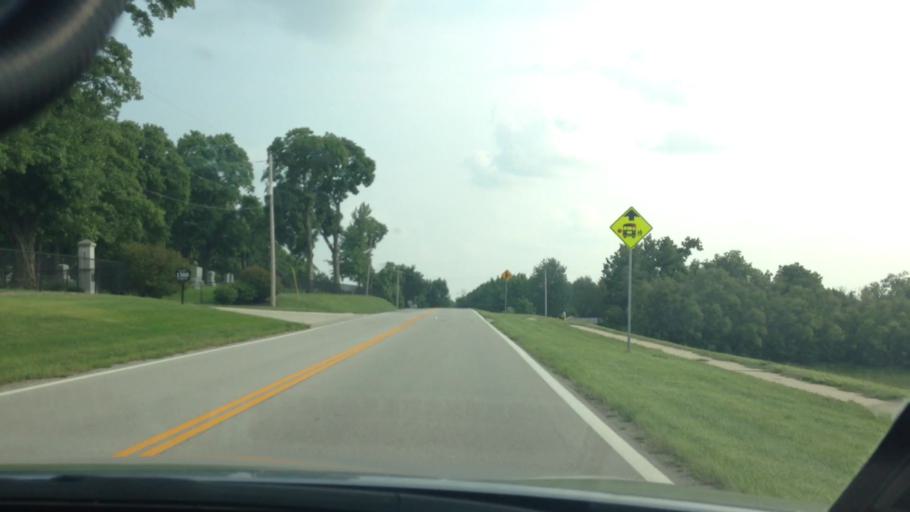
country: US
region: Kansas
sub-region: Leavenworth County
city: Lansing
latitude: 39.2724
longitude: -94.8905
